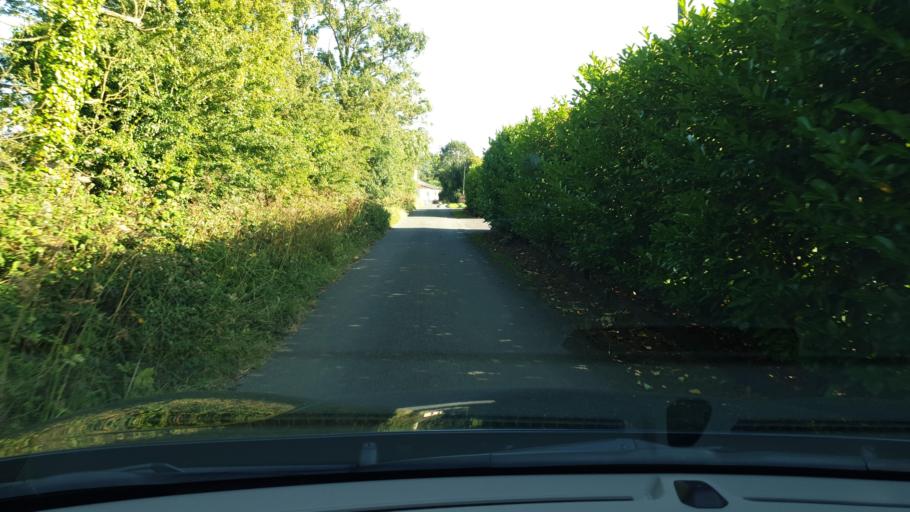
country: IE
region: Leinster
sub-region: An Mhi
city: Stamullin
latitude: 53.5884
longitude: -6.2526
